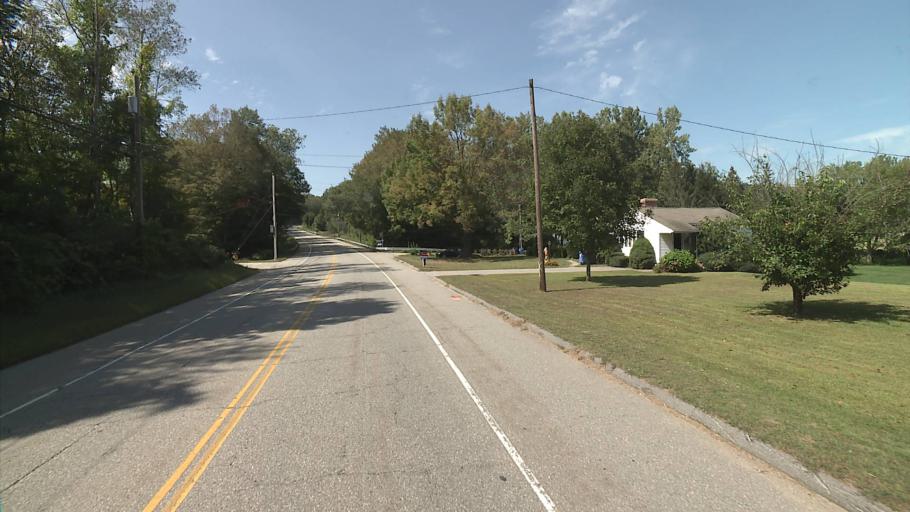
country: US
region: Connecticut
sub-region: New London County
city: Baltic
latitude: 41.5829
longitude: -72.1483
